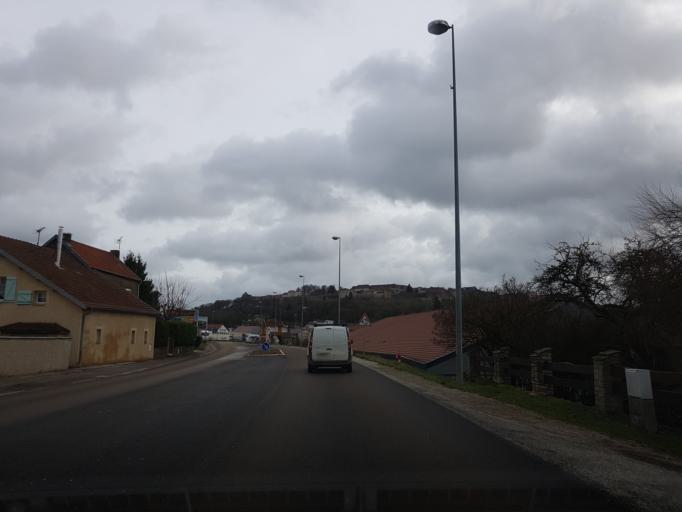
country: FR
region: Champagne-Ardenne
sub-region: Departement de la Haute-Marne
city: Langres
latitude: 47.8728
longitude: 5.3234
